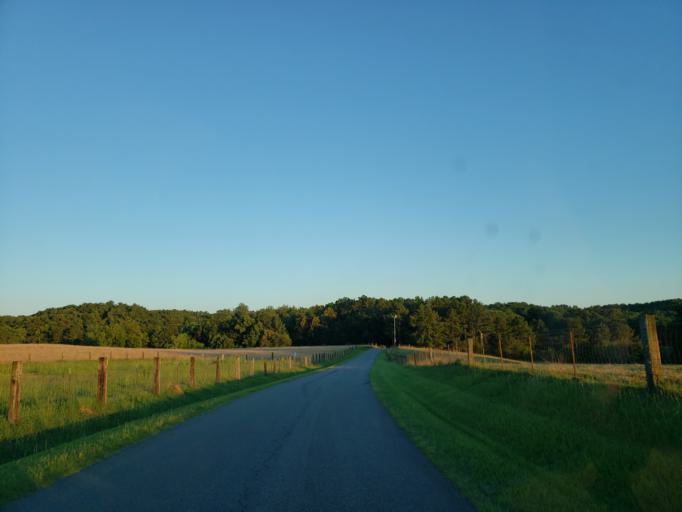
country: US
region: Georgia
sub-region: Bartow County
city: Euharlee
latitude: 34.0995
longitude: -84.8750
